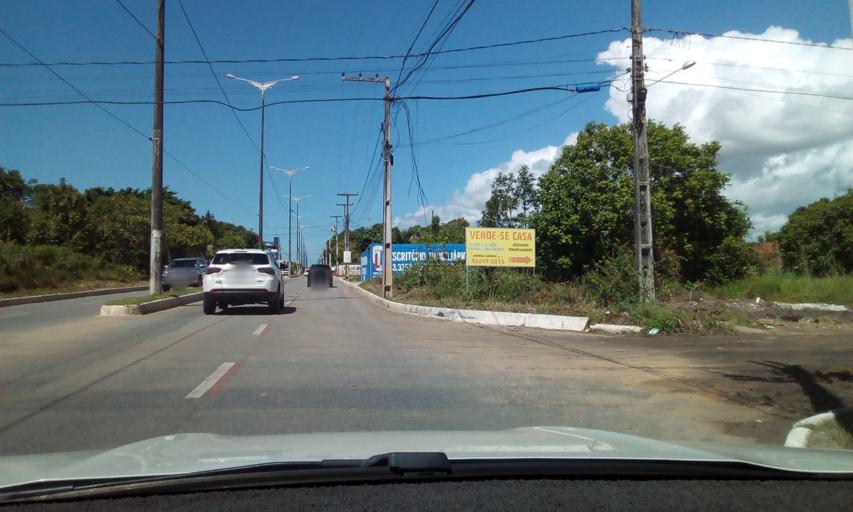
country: BR
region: Paraiba
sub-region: Joao Pessoa
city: Joao Pessoa
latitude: -7.1468
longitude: -34.8171
